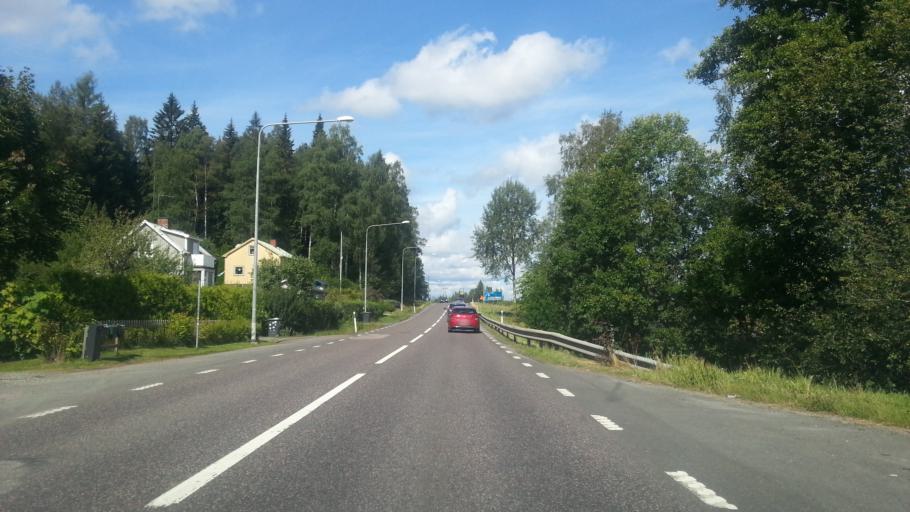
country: SE
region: Dalarna
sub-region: Ludvika Kommun
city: Ludvika
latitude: 60.1315
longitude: 15.1573
